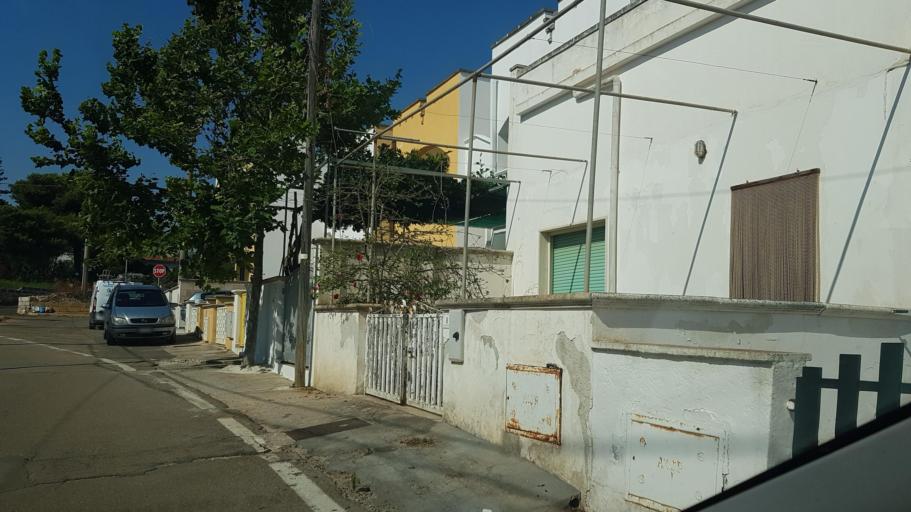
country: IT
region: Apulia
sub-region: Provincia di Lecce
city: Gemini
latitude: 39.8444
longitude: 18.2103
